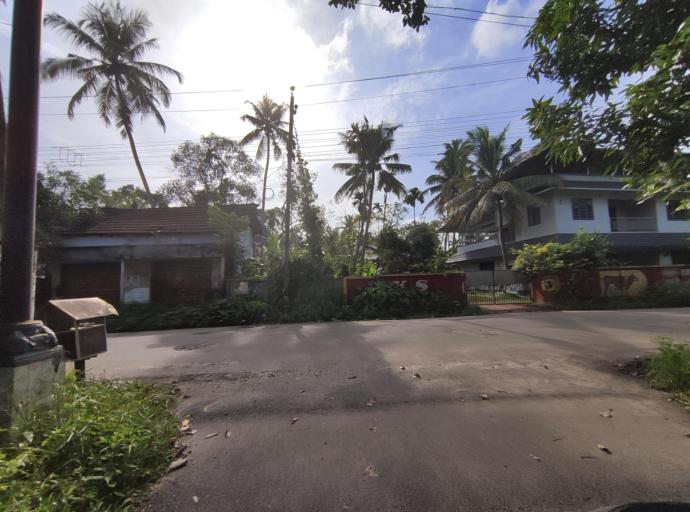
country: IN
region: Kerala
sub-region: Alappuzha
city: Vayalar
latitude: 9.6997
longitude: 76.3378
